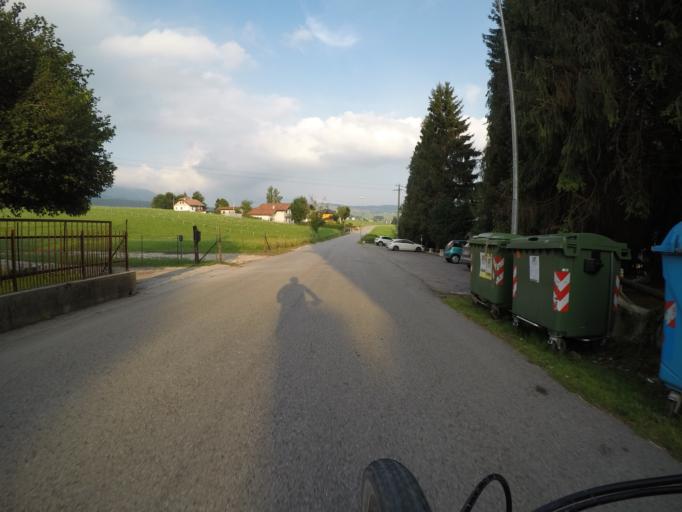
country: IT
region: Veneto
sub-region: Provincia di Vicenza
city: Asiago
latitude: 45.8847
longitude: 11.4993
